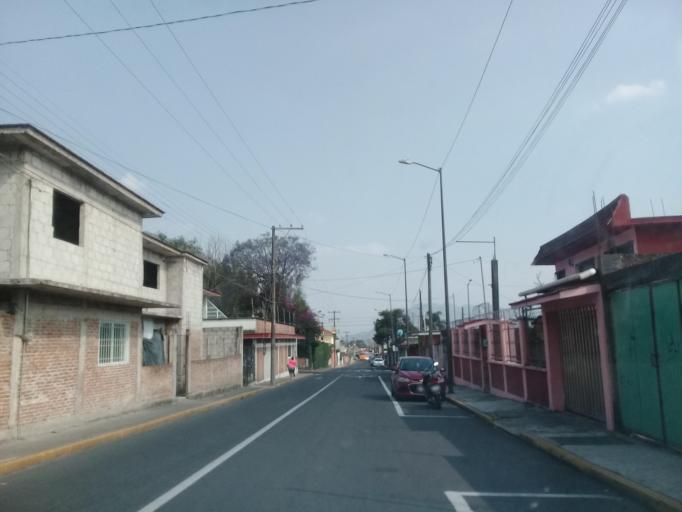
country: MX
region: Veracruz
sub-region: Ixhuatlancillo
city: Union y Progreso
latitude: 18.8683
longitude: -97.1032
